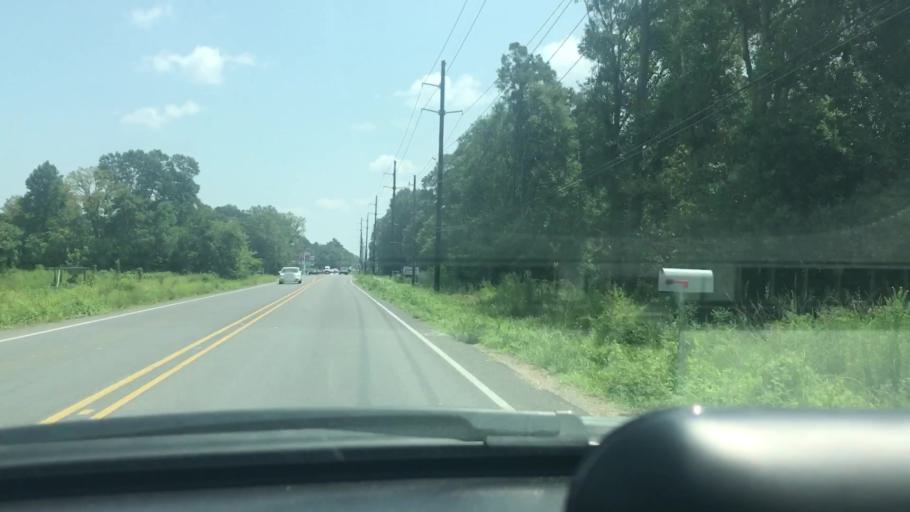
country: US
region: Louisiana
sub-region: Livingston Parish
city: Denham Springs
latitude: 30.4832
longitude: -90.9097
